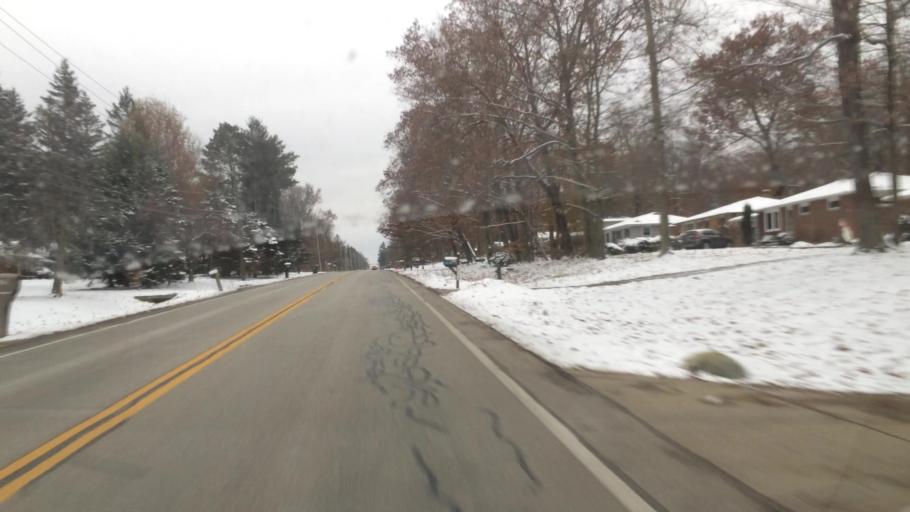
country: US
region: Ohio
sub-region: Cuyahoga County
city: Strongsville
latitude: 41.3003
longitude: -81.7853
